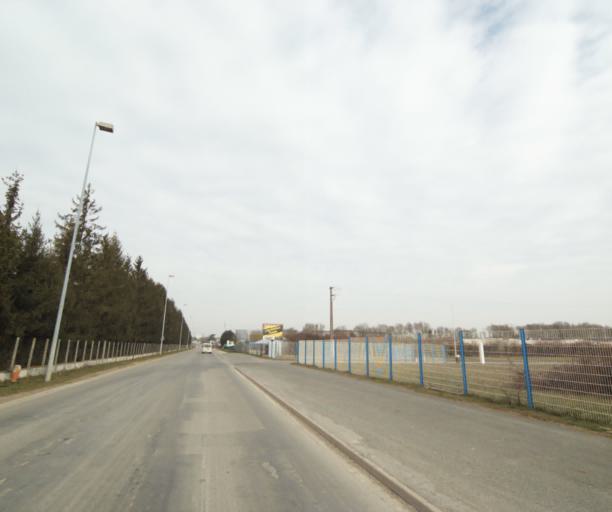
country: FR
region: Poitou-Charentes
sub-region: Departement des Deux-Sevres
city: Niort
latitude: 46.3005
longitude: -0.4601
